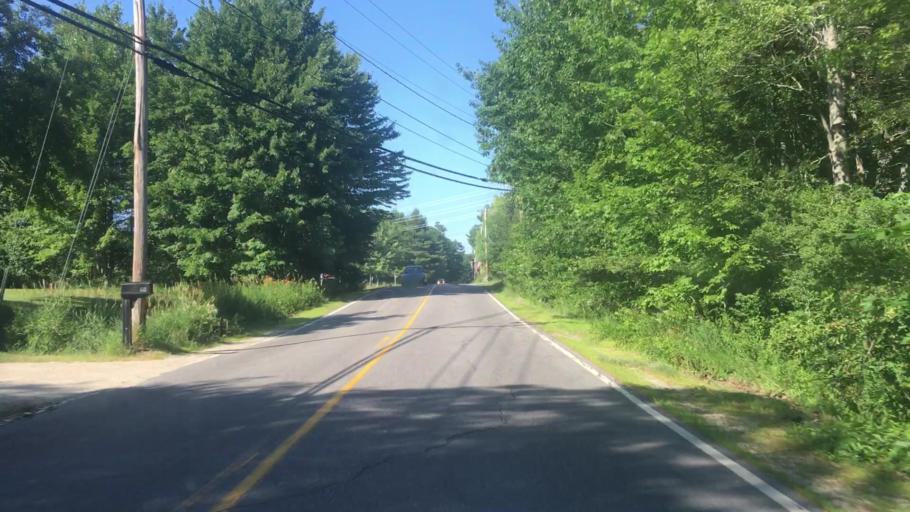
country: US
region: Maine
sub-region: York County
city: Hollis Center
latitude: 43.6698
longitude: -70.5995
